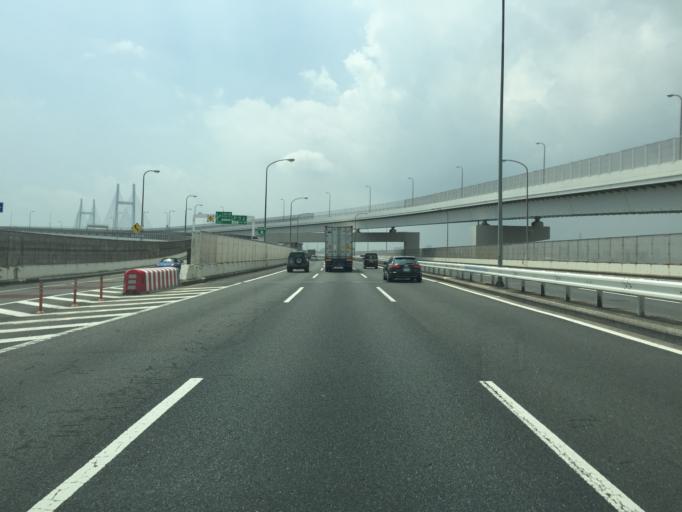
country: JP
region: Kanagawa
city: Yokohama
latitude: 35.4656
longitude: 139.6849
